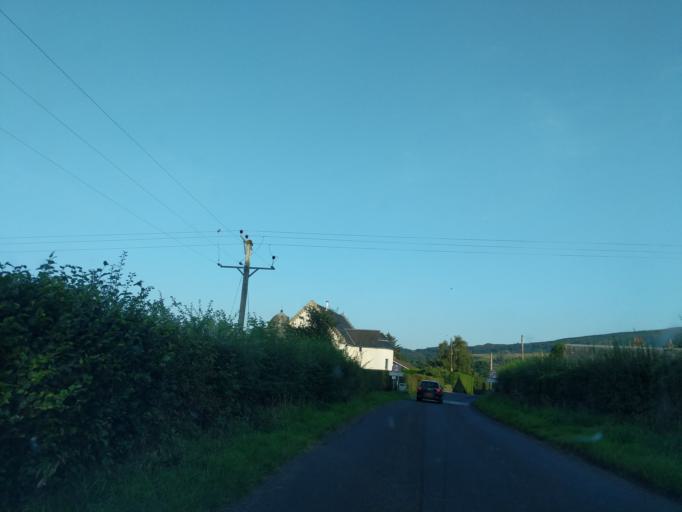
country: GB
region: Scotland
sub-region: Stirling
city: Doune
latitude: 56.1270
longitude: -4.0865
